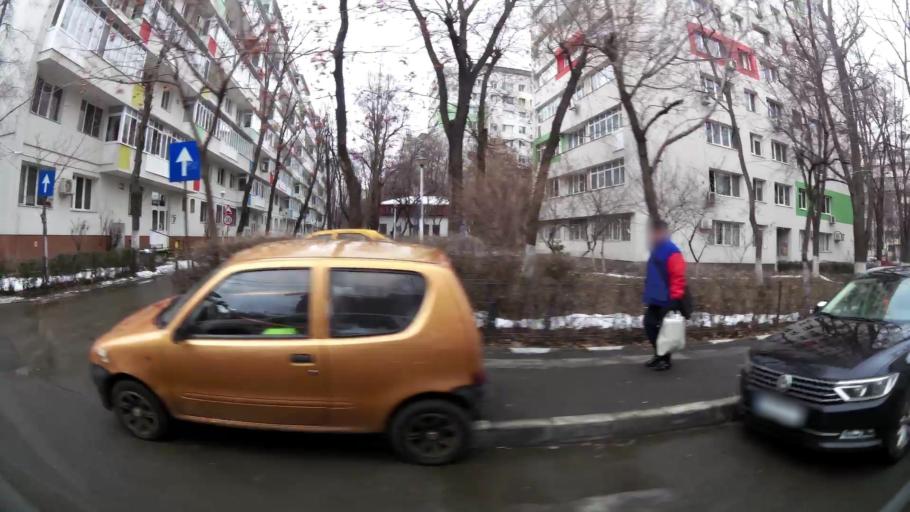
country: RO
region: Ilfov
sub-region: Comuna Chiajna
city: Rosu
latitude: 44.4689
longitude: 26.0575
